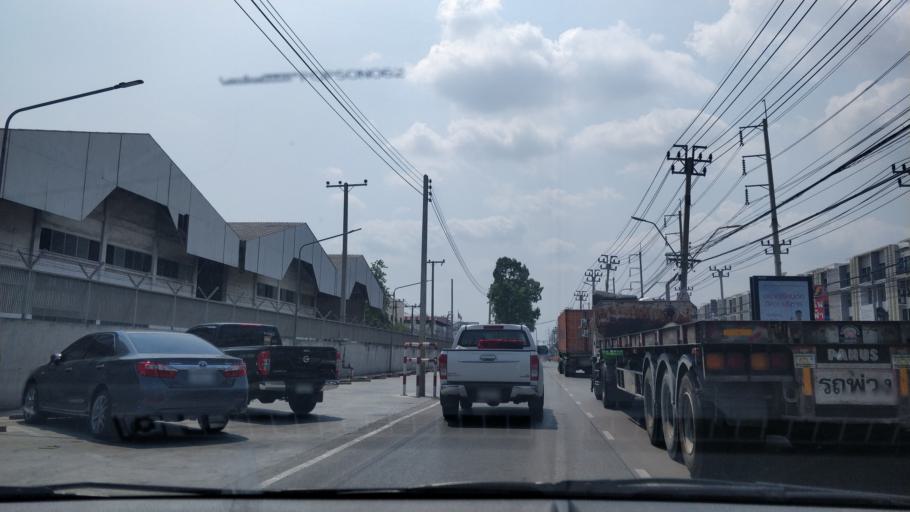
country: TH
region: Bangkok
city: Lat Krabang
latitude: 13.7563
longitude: 100.7961
